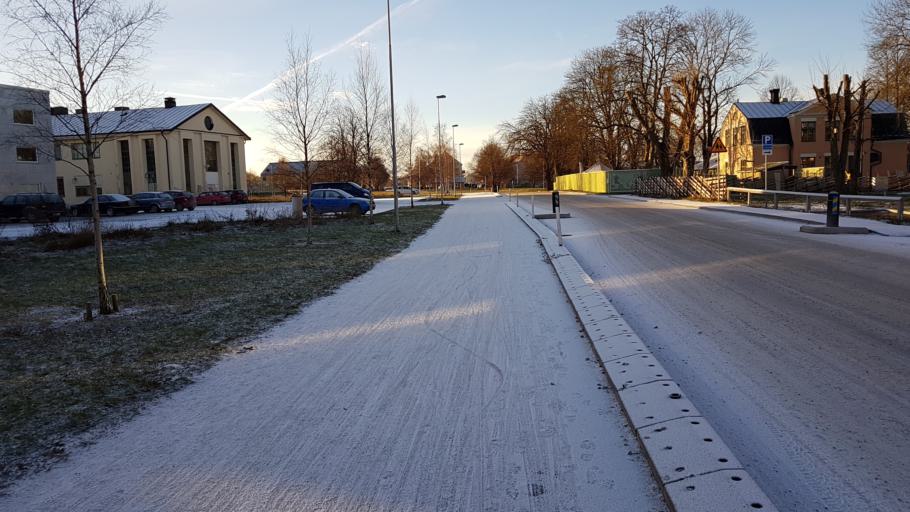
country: SE
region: Gotland
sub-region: Gotland
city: Visby
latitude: 57.6323
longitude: 18.3044
